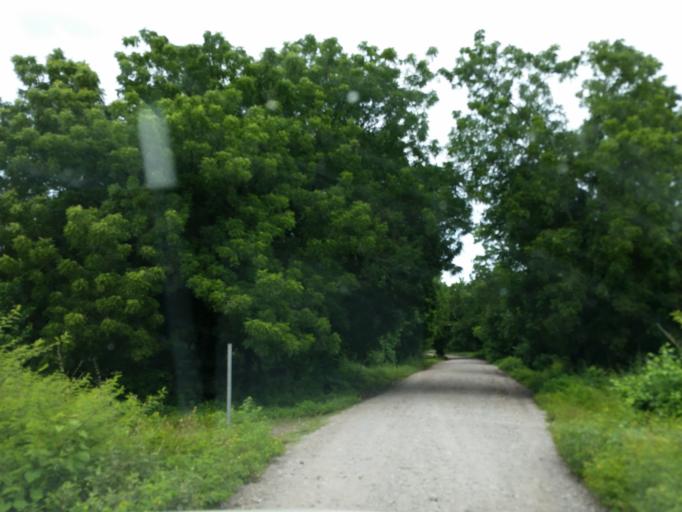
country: NI
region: Leon
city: Telica
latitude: 12.7166
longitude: -86.8756
